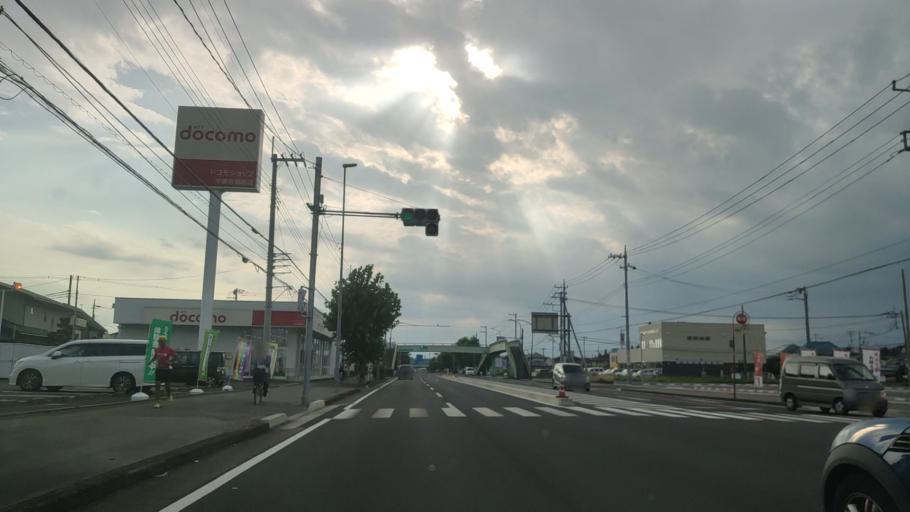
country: JP
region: Tochigi
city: Utsunomiya-shi
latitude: 36.5497
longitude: 139.8562
